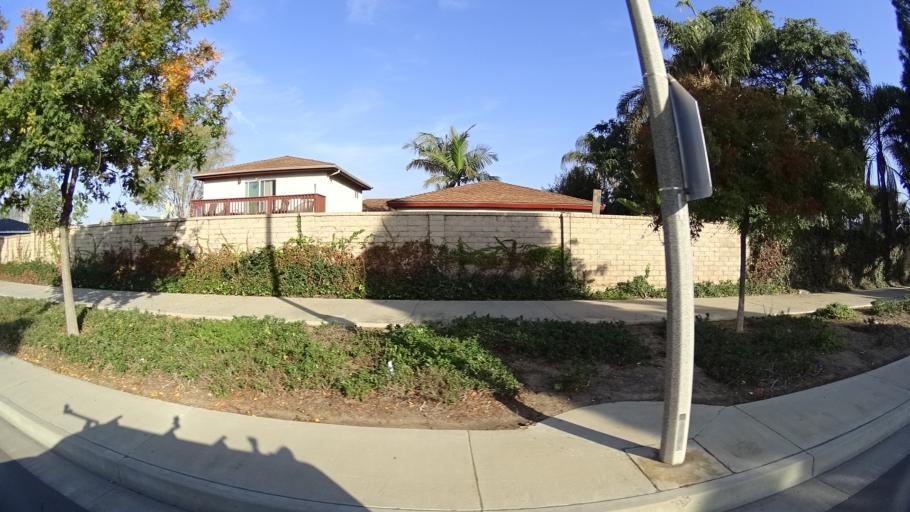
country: US
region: California
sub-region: Orange County
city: Costa Mesa
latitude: 33.6526
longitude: -117.9388
